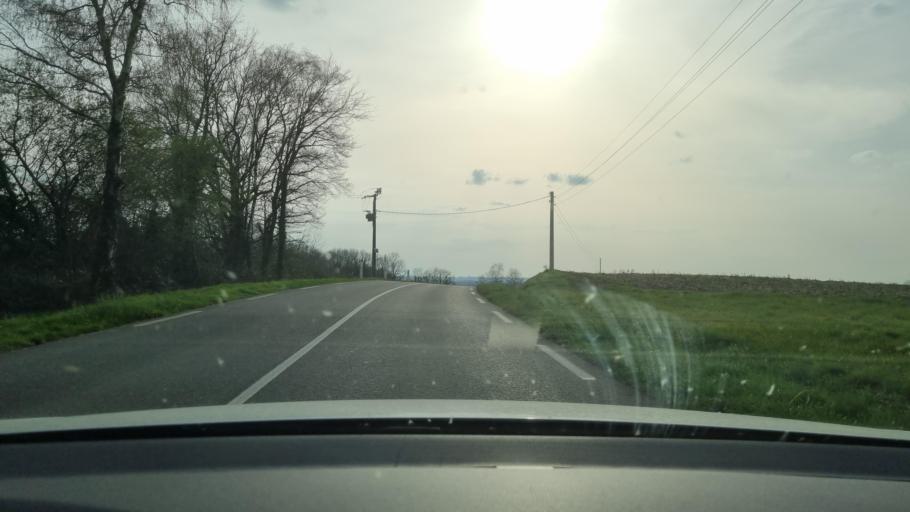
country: FR
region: Aquitaine
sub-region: Departement des Pyrenees-Atlantiques
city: Morlaas
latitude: 43.3680
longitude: -0.1898
